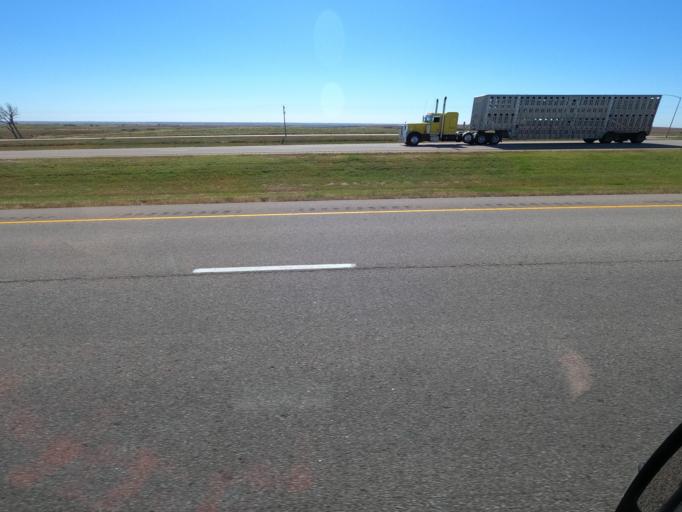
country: US
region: Kansas
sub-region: Russell County
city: Russell
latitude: 38.8576
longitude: -98.7037
